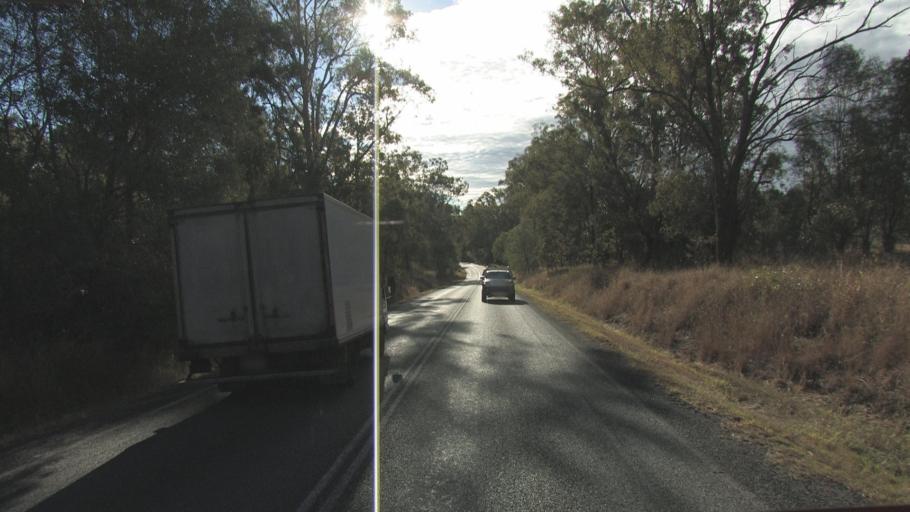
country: AU
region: Queensland
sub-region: Logan
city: Cedar Vale
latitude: -27.8881
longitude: 153.0817
